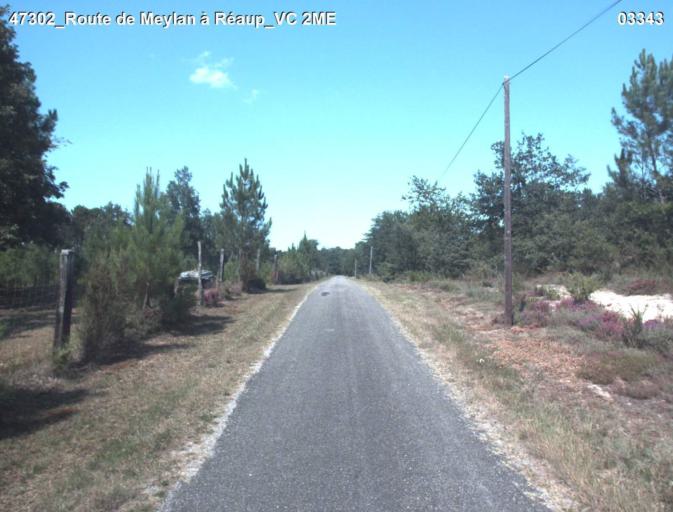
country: FR
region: Aquitaine
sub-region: Departement du Lot-et-Garonne
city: Mezin
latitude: 44.0805
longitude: 0.1244
